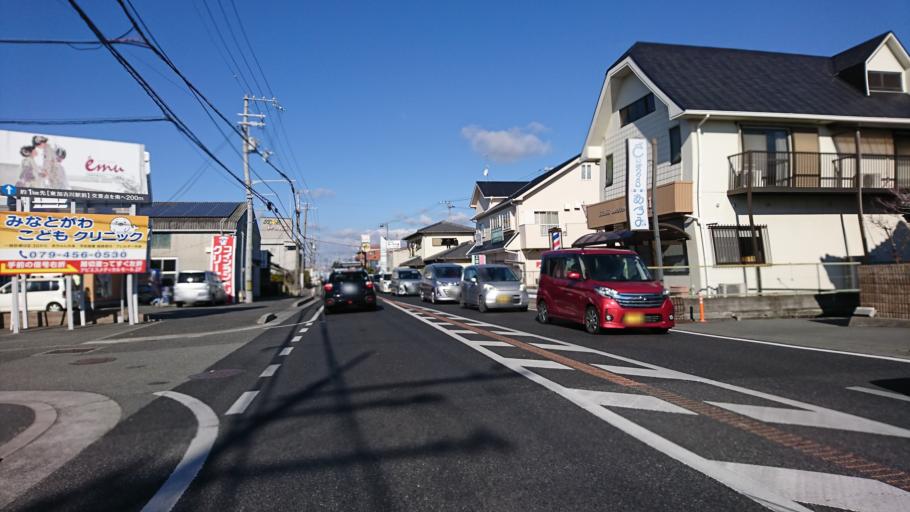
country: JP
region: Hyogo
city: Kakogawacho-honmachi
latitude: 34.7353
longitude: 134.8754
